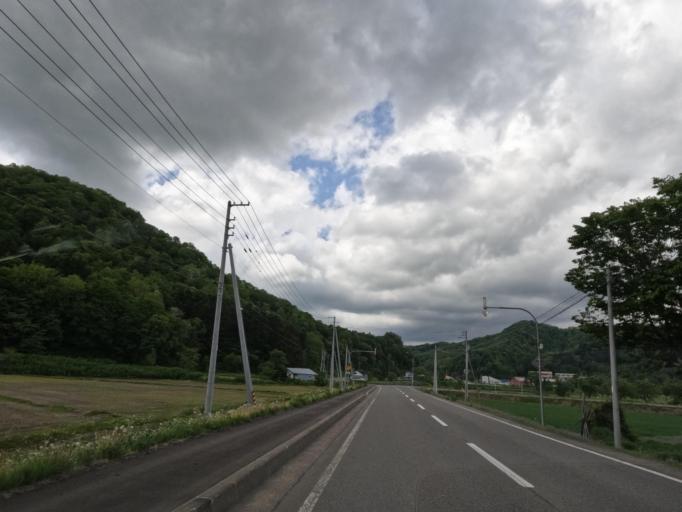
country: JP
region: Hokkaido
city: Takikawa
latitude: 43.5896
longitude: 141.7325
